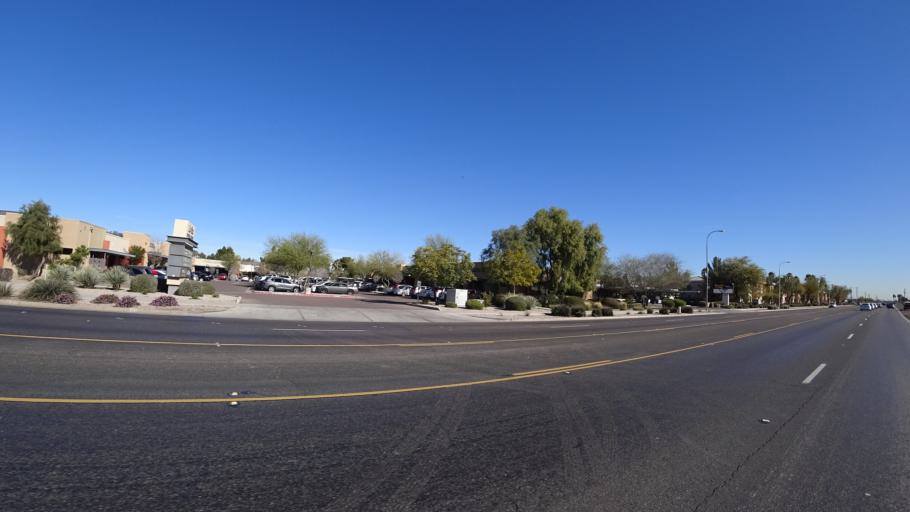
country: US
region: Arizona
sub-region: Maricopa County
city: Tolleson
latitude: 33.4936
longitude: -112.2807
